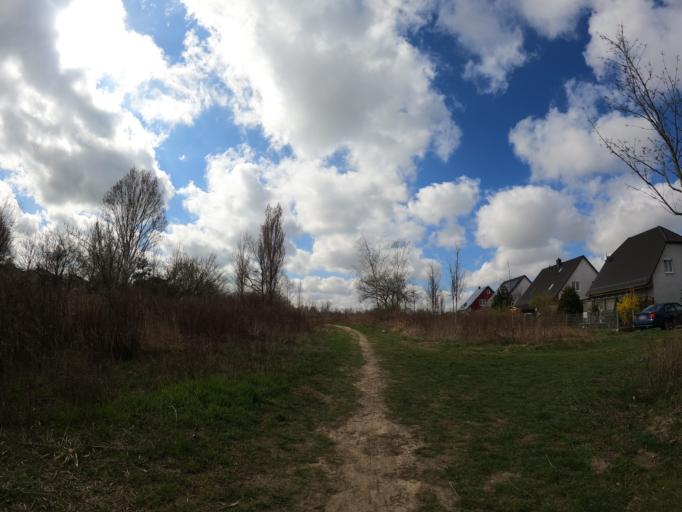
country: DE
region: Berlin
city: Mahlsdorf
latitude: 52.5190
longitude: 13.6370
